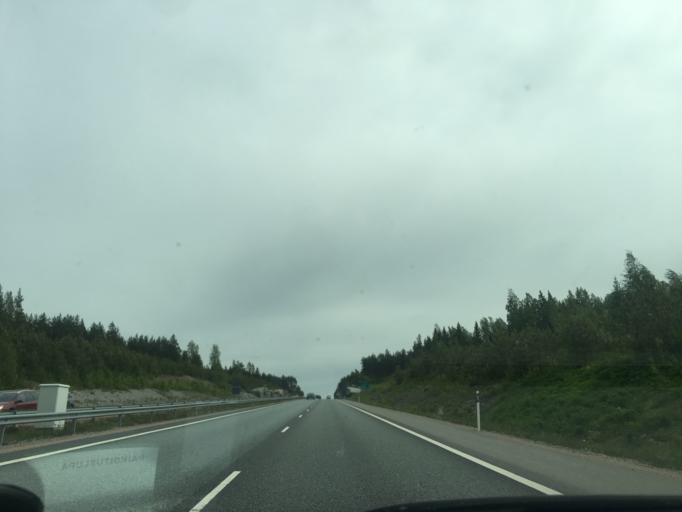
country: FI
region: Varsinais-Suomi
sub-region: Salo
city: Suomusjaervi
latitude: 60.3781
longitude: 23.6314
